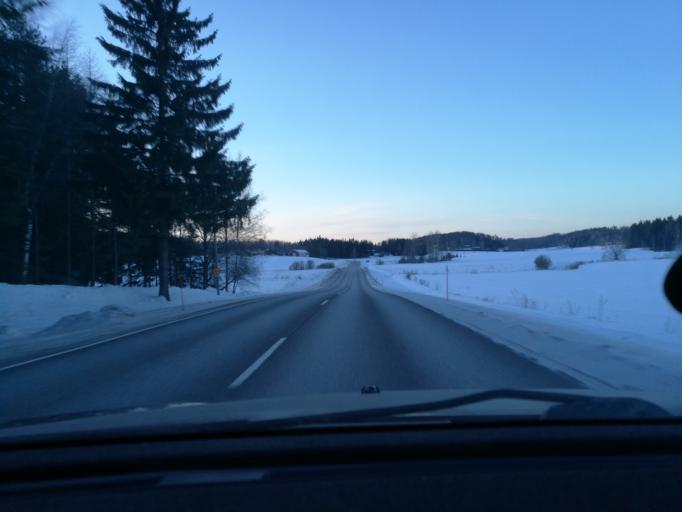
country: FI
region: Uusimaa
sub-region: Helsinki
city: Vihti
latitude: 60.4302
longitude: 24.4265
